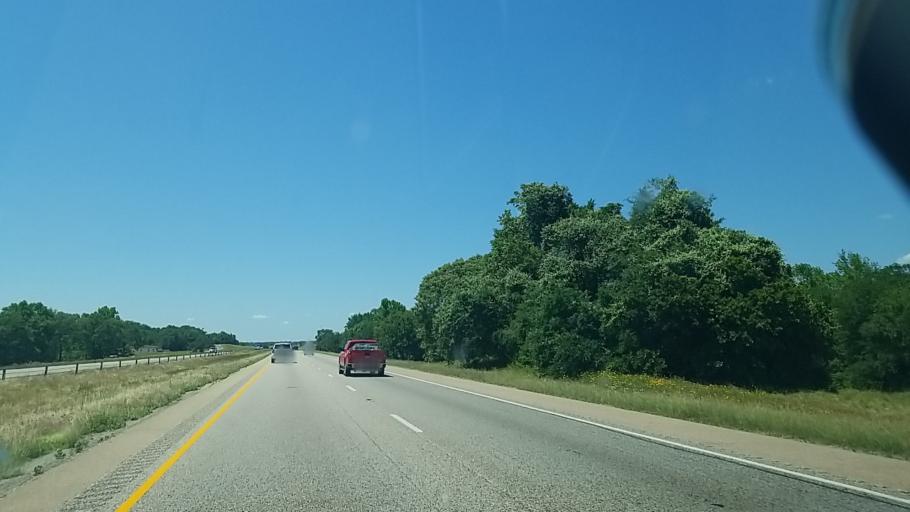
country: US
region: Texas
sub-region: Leon County
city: Buffalo
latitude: 31.3953
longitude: -96.0318
